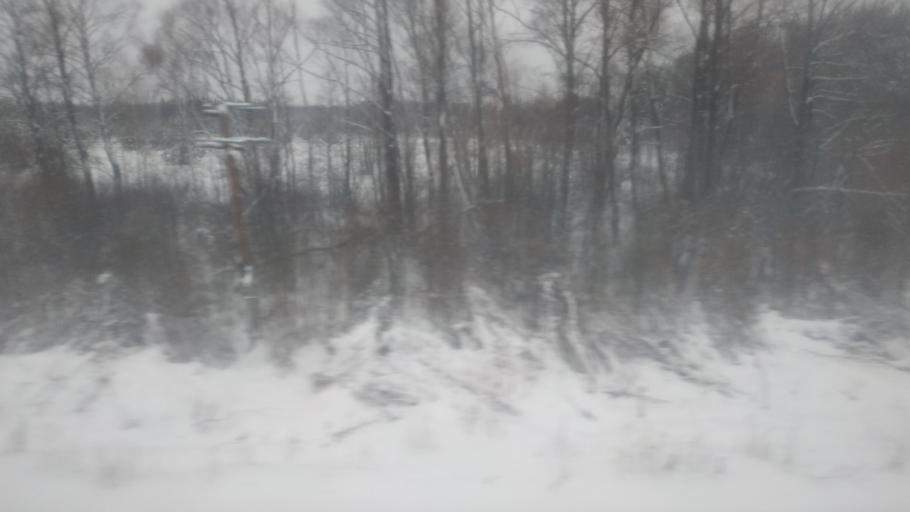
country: RU
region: Bashkortostan
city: Yanaul
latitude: 56.2519
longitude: 54.6963
